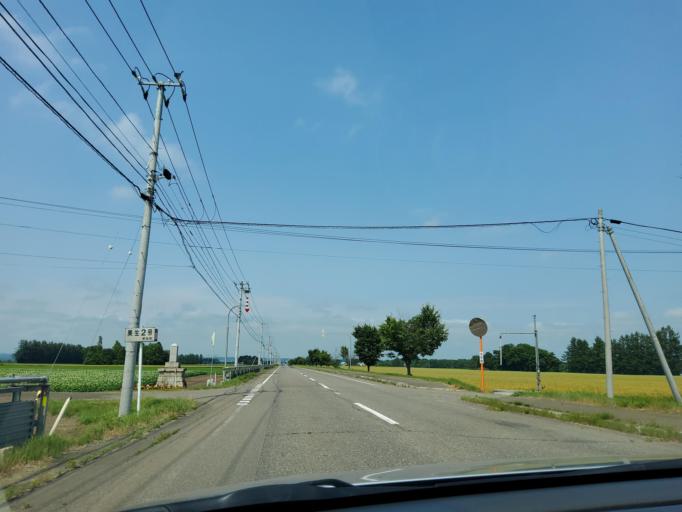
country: JP
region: Hokkaido
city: Obihiro
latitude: 42.8811
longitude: 143.0321
